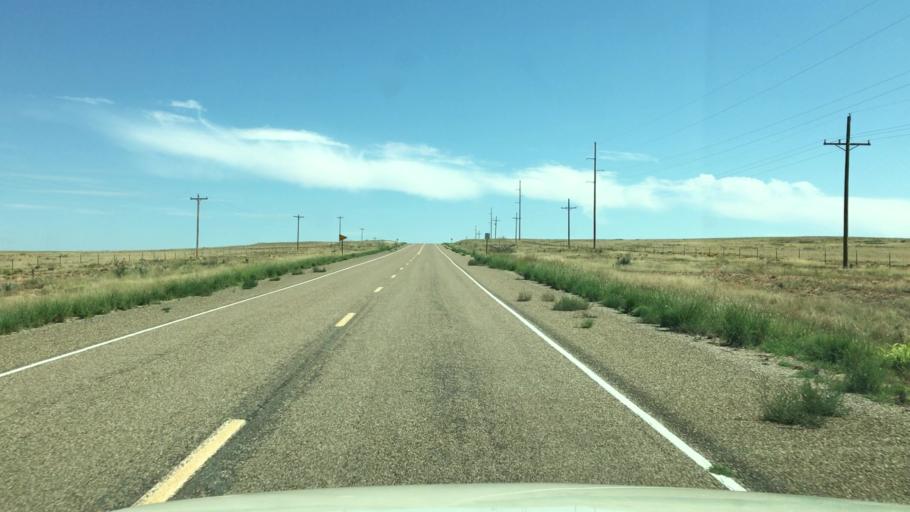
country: US
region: New Mexico
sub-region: Chaves County
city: Roswell
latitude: 33.9342
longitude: -104.5955
